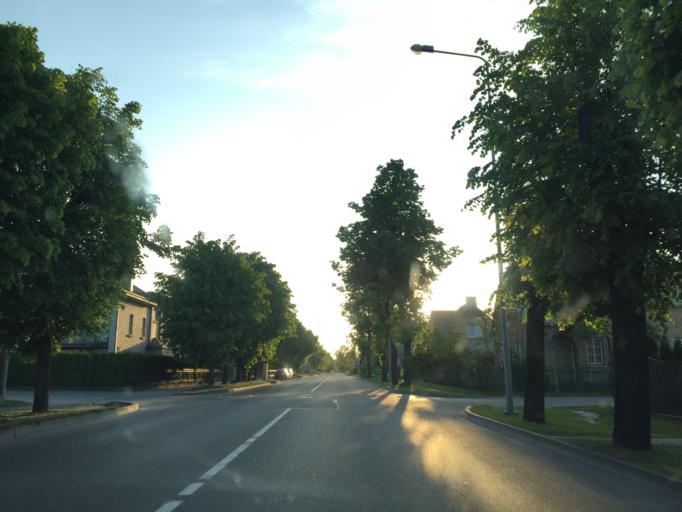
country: LT
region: Siauliu apskritis
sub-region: Siauliai
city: Siauliai
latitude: 55.9542
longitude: 23.3320
